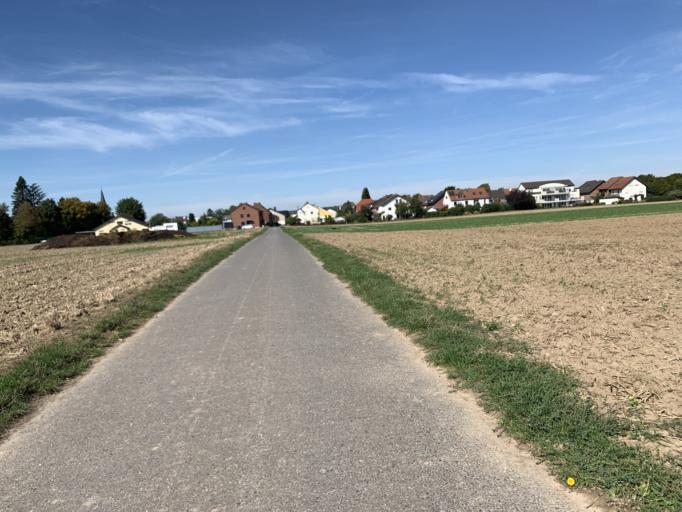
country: DE
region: North Rhine-Westphalia
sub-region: Regierungsbezirk Koln
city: Dueren
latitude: 50.7906
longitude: 6.4521
